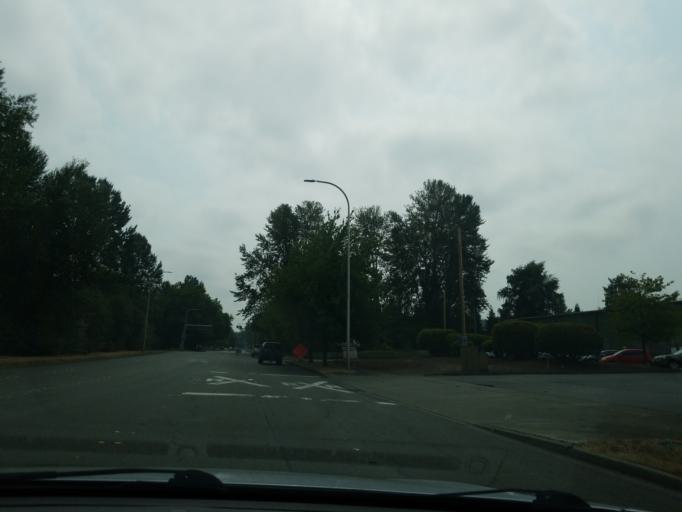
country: US
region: Washington
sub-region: King County
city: Tukwila
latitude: 47.4461
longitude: -122.2328
